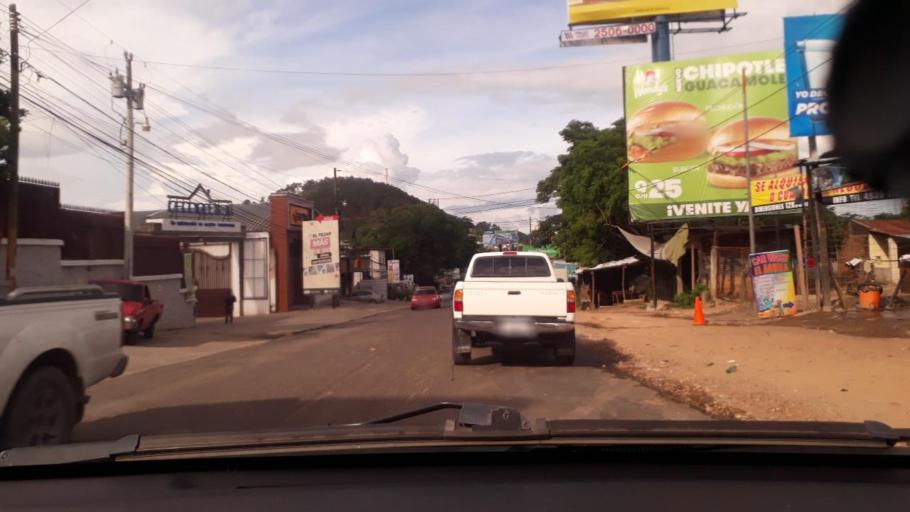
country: GT
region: Jutiapa
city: Jutiapa
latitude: 14.2932
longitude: -89.9131
